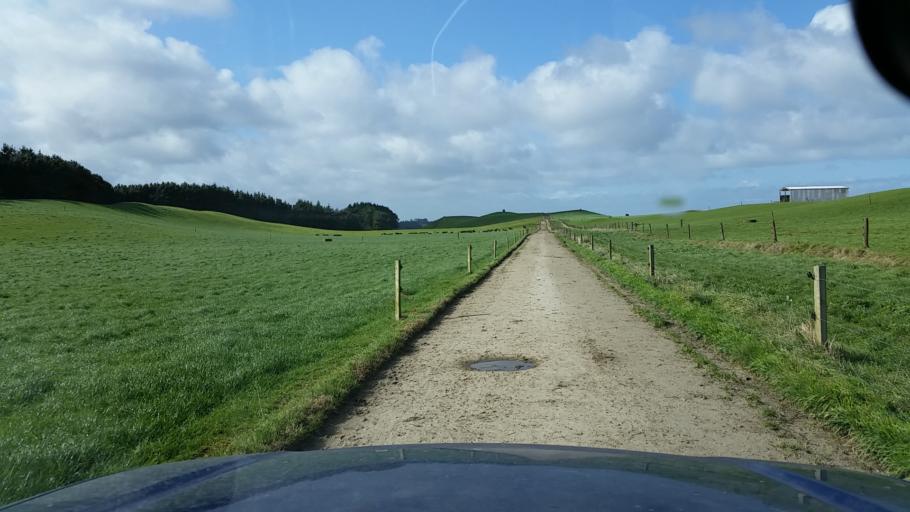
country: NZ
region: Taranaki
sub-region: South Taranaki District
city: Patea
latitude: -39.7427
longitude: 174.5322
